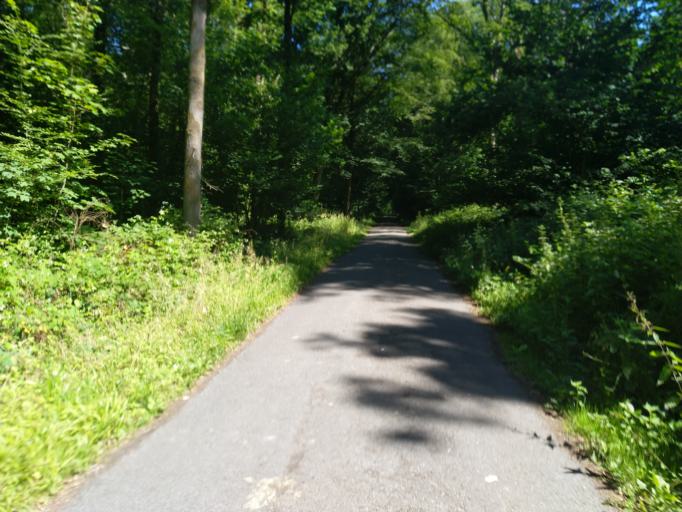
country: BE
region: Wallonia
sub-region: Province du Hainaut
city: Colfontaine
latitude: 50.3797
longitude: 3.8493
